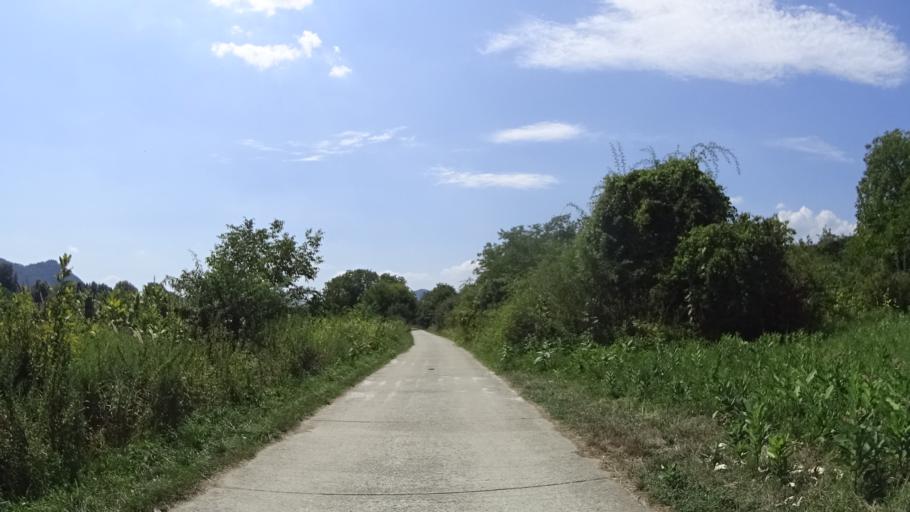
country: HU
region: Pest
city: Kismaros
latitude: 47.8172
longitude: 18.9842
